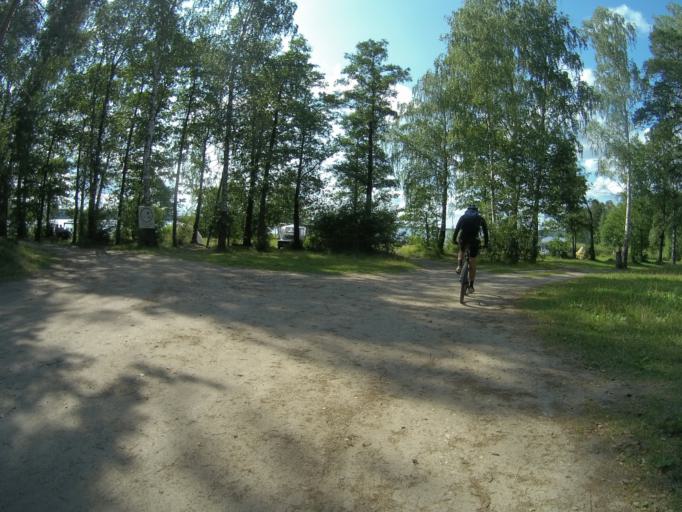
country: RU
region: Ivanovo
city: Novoye Leushino
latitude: 56.7221
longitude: 40.6270
